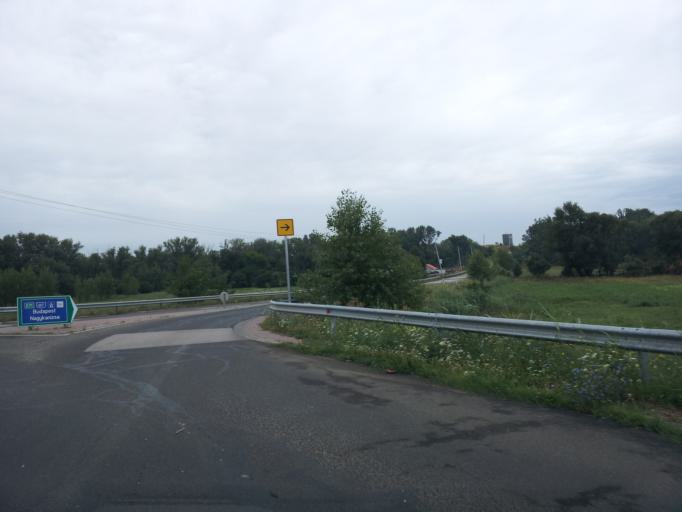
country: HU
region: Pest
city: Tarnok
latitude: 47.3929
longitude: 18.8482
